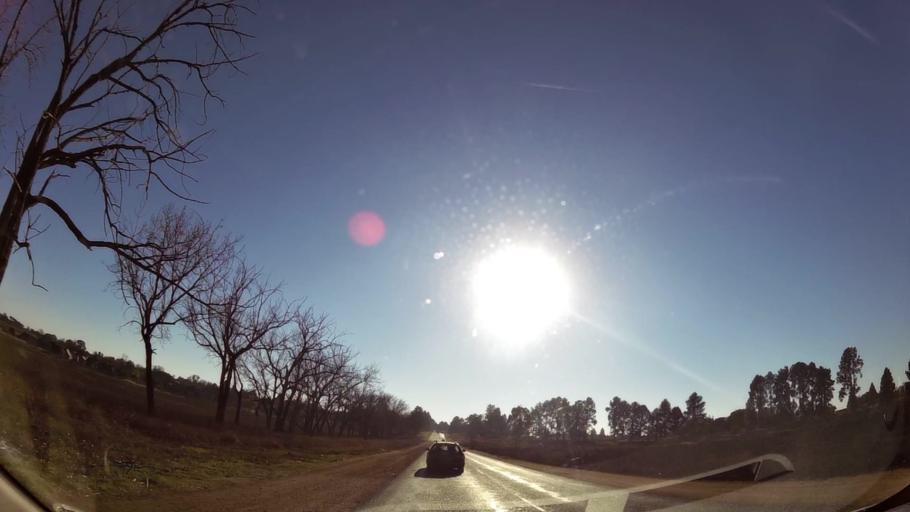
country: ZA
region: Gauteng
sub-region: Ekurhuleni Metropolitan Municipality
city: Tembisa
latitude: -26.0444
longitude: 28.2448
